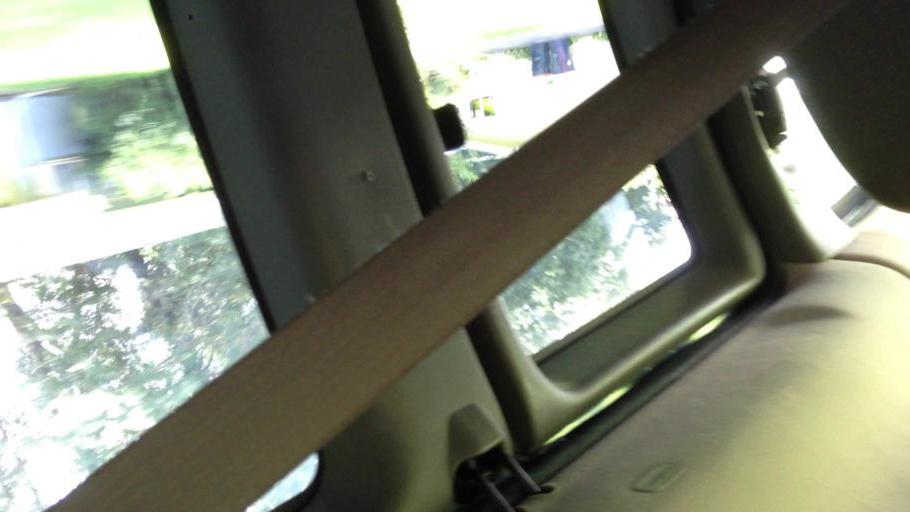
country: US
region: New York
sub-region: Dutchess County
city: Red Hook
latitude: 42.0209
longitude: -73.8831
